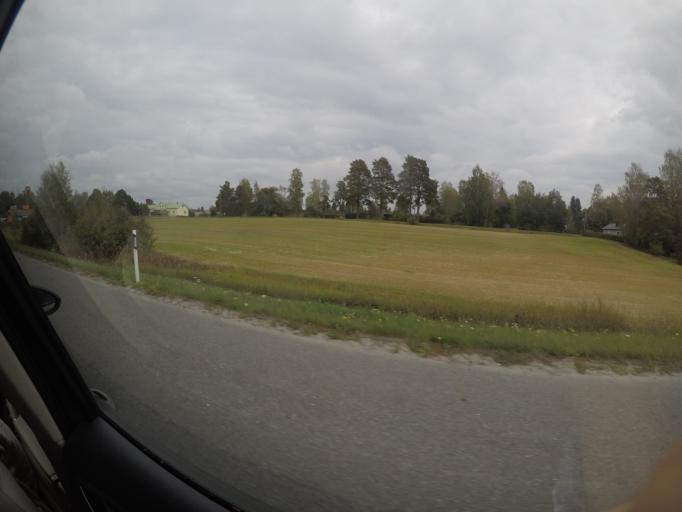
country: FI
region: Haeme
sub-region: Haemeenlinna
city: Parola
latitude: 61.0552
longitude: 24.3931
